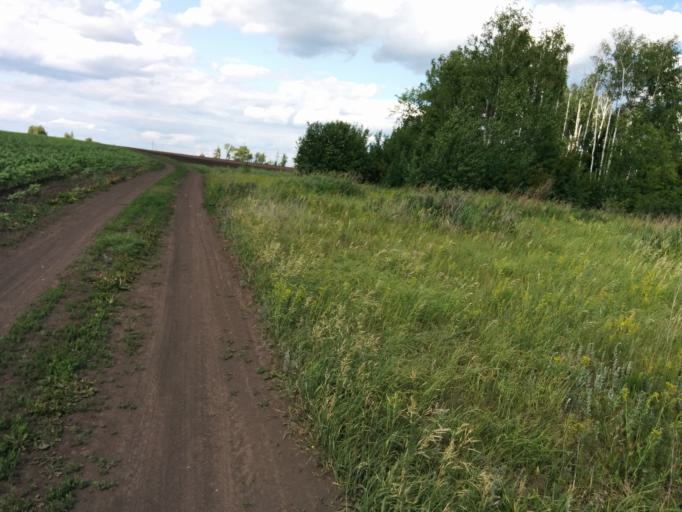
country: RU
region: Tambov
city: Donskoye
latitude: 52.8083
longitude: 41.3964
